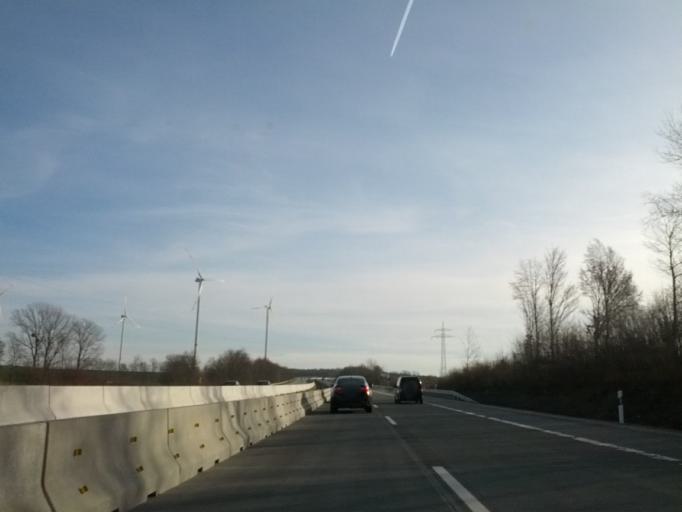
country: DE
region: Bavaria
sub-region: Regierungsbezirk Mittelfranken
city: Gollhofen
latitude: 49.5374
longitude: 10.1741
